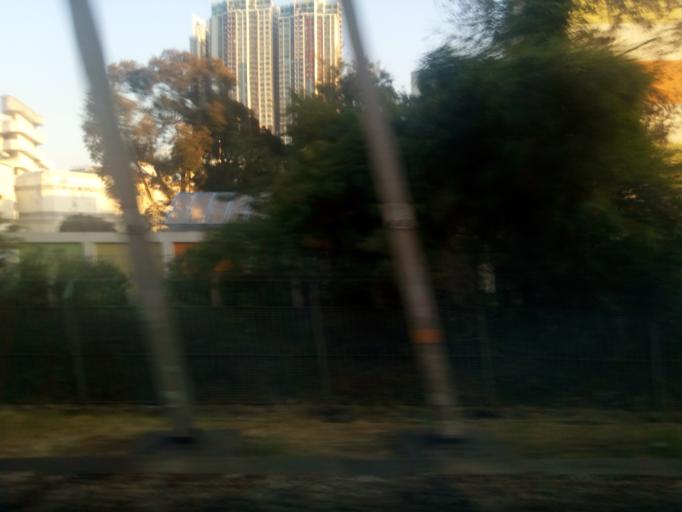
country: HK
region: Sha Tin
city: Sha Tin
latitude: 22.3766
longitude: 114.1827
